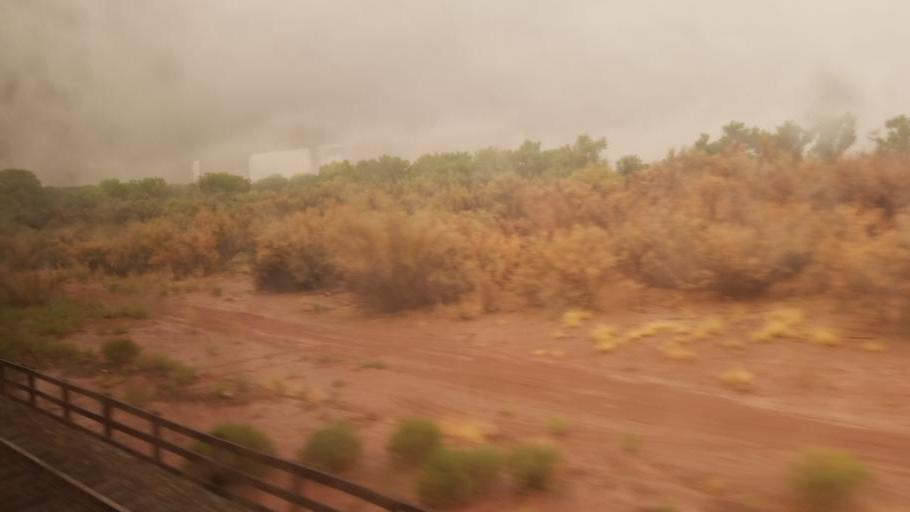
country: US
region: Arizona
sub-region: Navajo County
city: Holbrook
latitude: 34.9036
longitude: -110.2370
